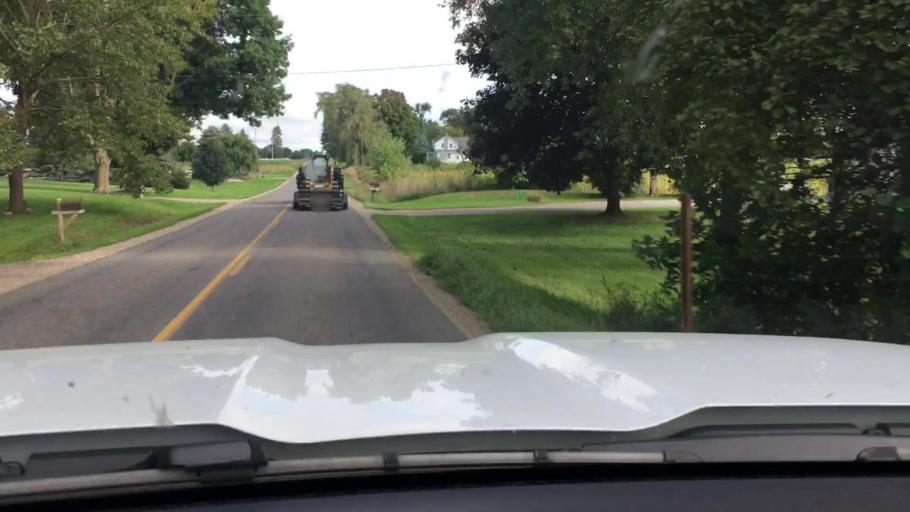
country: US
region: Michigan
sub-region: Kent County
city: Byron Center
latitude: 42.8002
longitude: -85.8027
